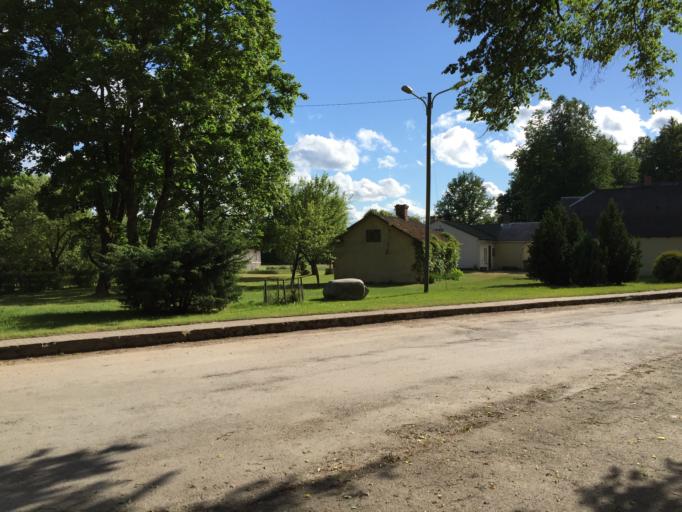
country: LV
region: Vecumnieki
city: Vecumnieki
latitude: 56.4518
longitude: 24.5991
